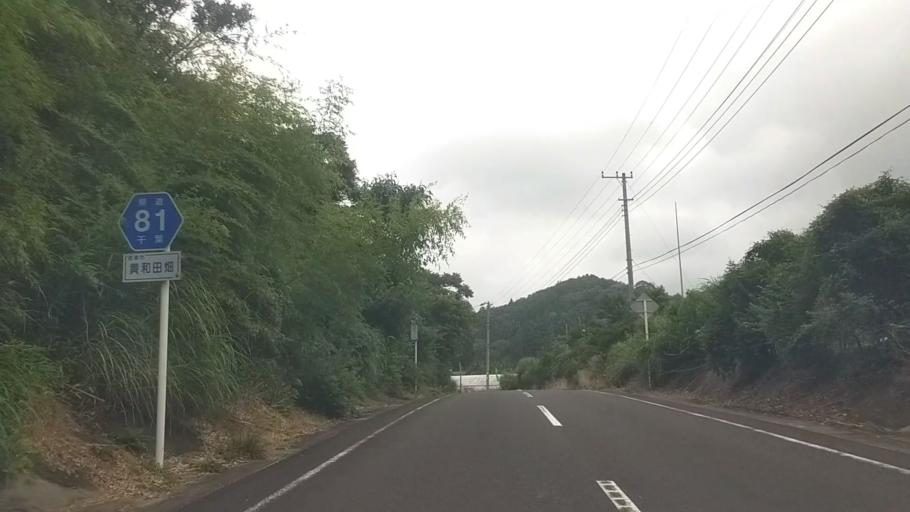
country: JP
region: Chiba
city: Kawaguchi
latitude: 35.1911
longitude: 140.1387
